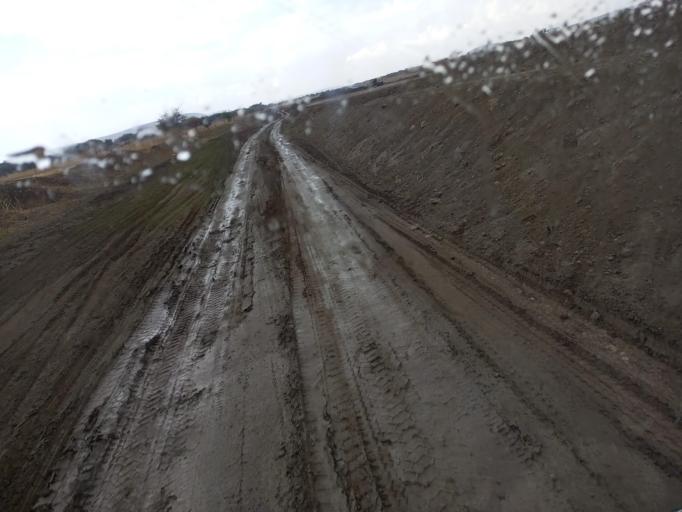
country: ET
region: Oromiya
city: Ziway
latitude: 7.7575
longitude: 38.6109
